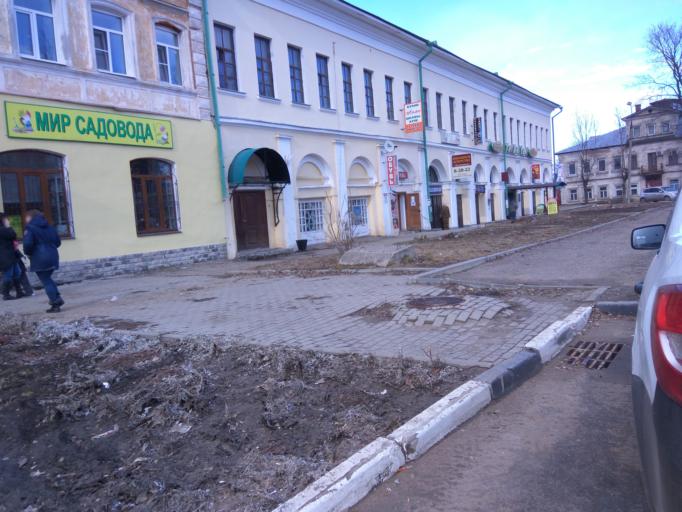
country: RU
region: Jaroslavl
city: Rostov
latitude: 57.1867
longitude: 39.4189
